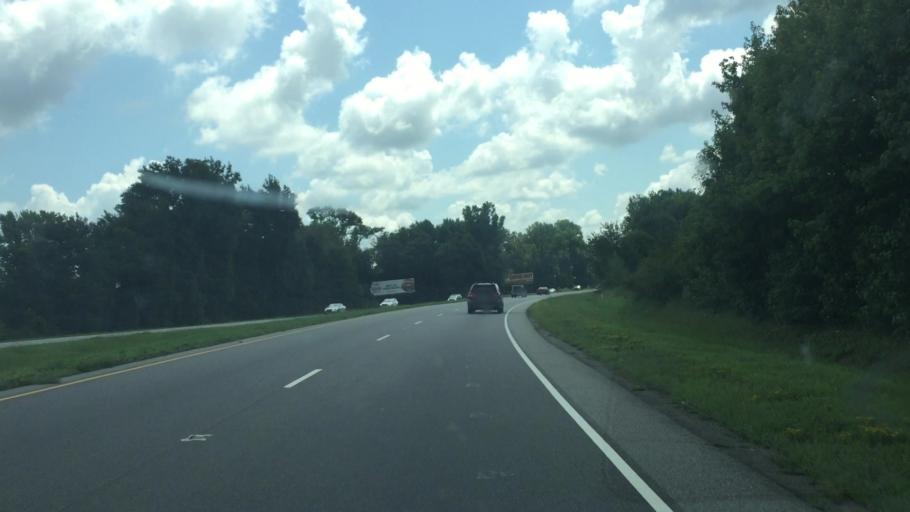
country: US
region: North Carolina
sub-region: Scotland County
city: Laurel Hill
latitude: 34.7985
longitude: -79.5210
